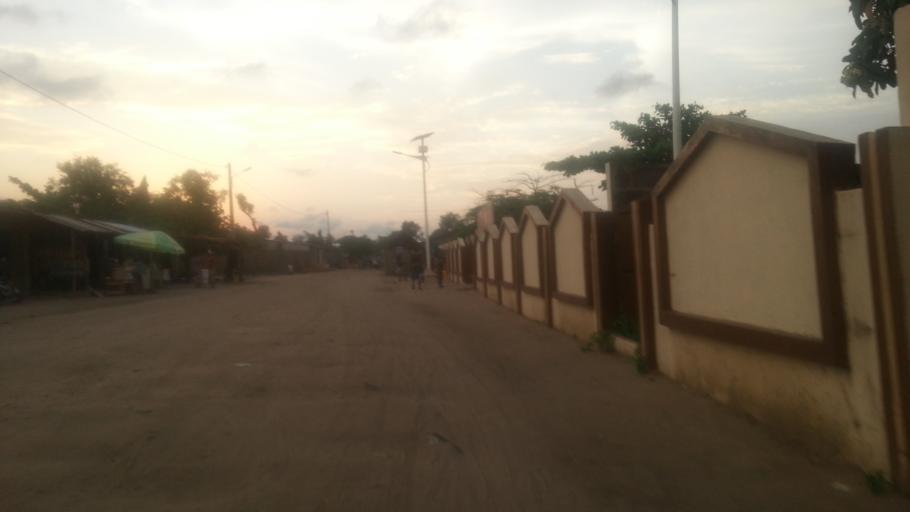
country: BJ
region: Queme
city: Porto-Novo
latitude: 6.3874
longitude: 2.5424
